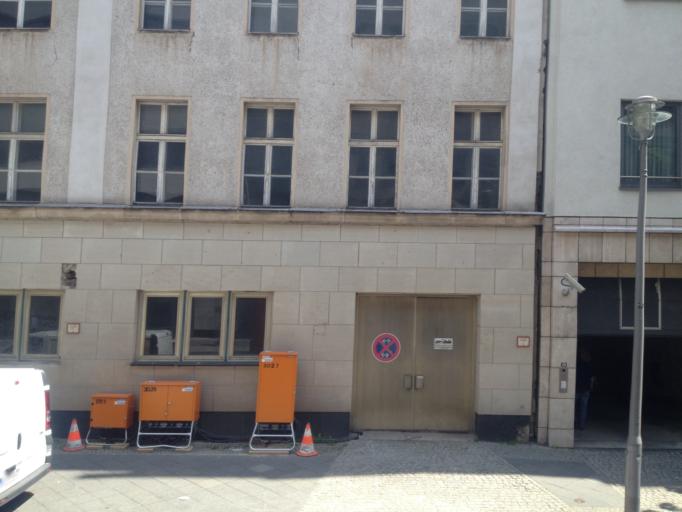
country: DE
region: Berlin
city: Tiergarten Bezirk
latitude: 52.5173
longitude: 13.3806
